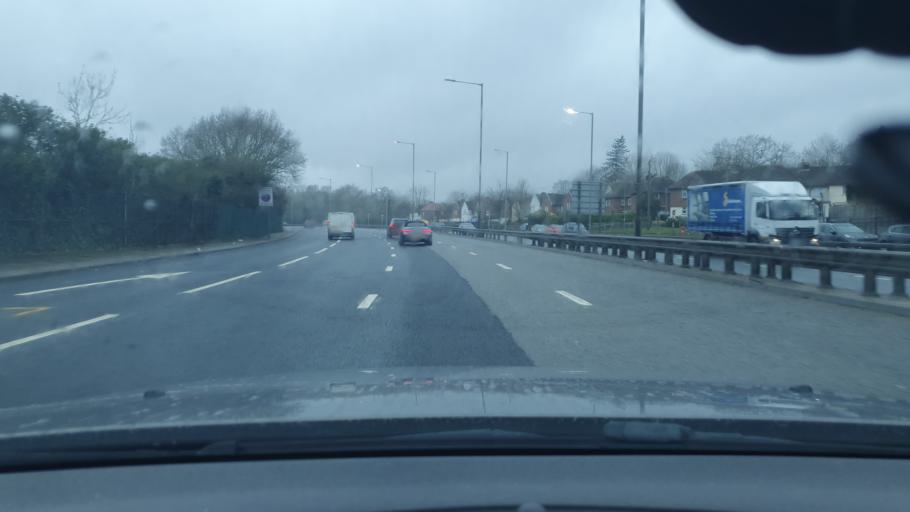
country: GB
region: England
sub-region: Greater London
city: Wood Green
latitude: 51.6057
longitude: -0.1591
